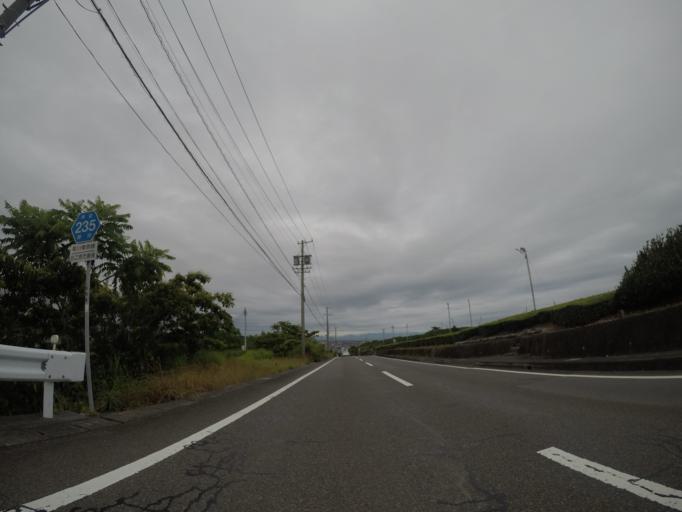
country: JP
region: Shizuoka
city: Sagara
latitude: 34.7374
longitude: 138.2074
